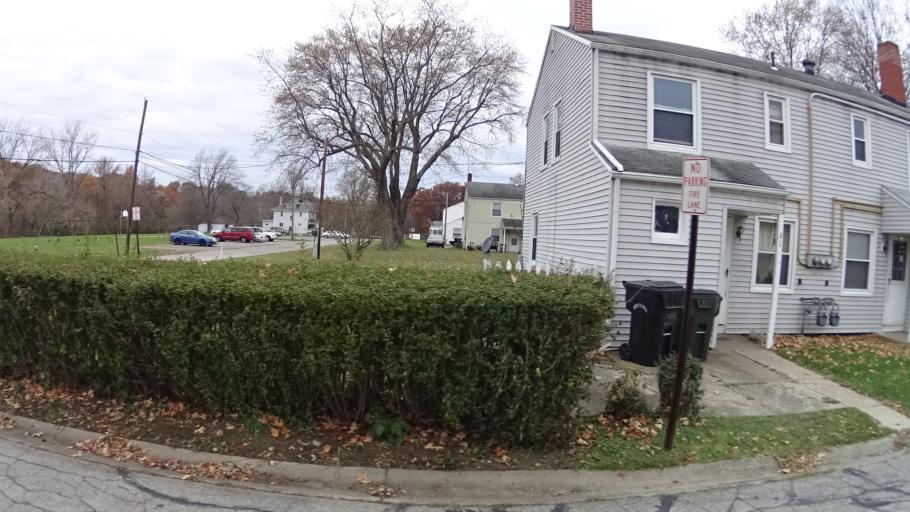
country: US
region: Ohio
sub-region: Lorain County
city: Elyria
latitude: 41.3513
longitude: -82.1117
